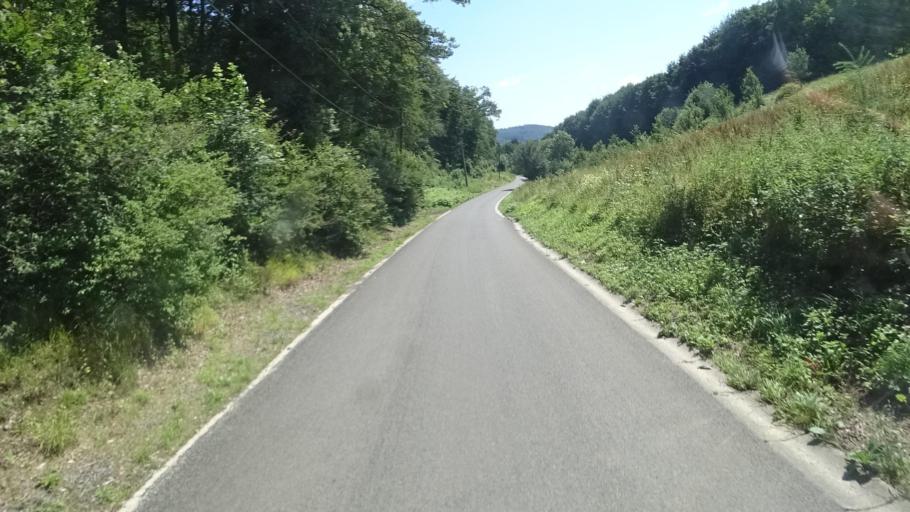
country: BE
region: Wallonia
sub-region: Province de Namur
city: Profondeville
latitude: 50.3503
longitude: 4.8425
